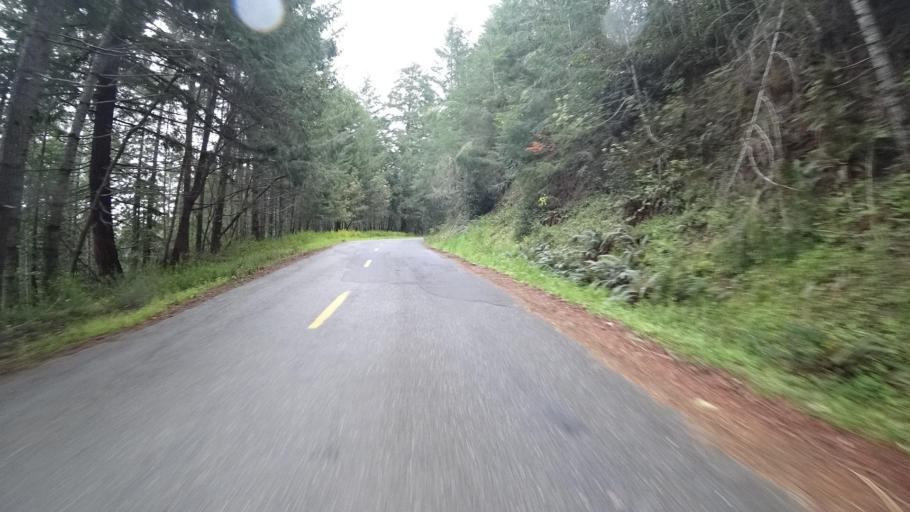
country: US
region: California
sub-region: Humboldt County
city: Redway
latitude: 40.2783
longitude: -123.7933
